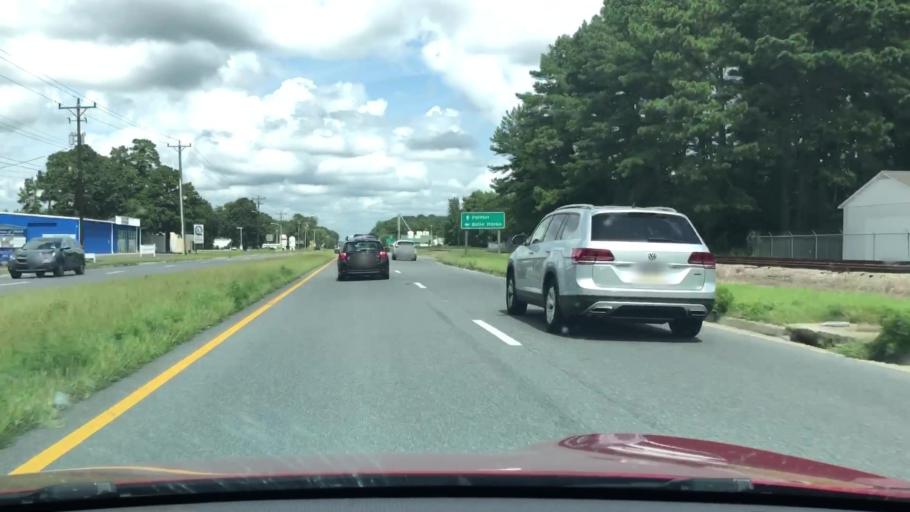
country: US
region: Virginia
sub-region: Northampton County
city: Exmore
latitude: 37.5487
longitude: -75.8138
